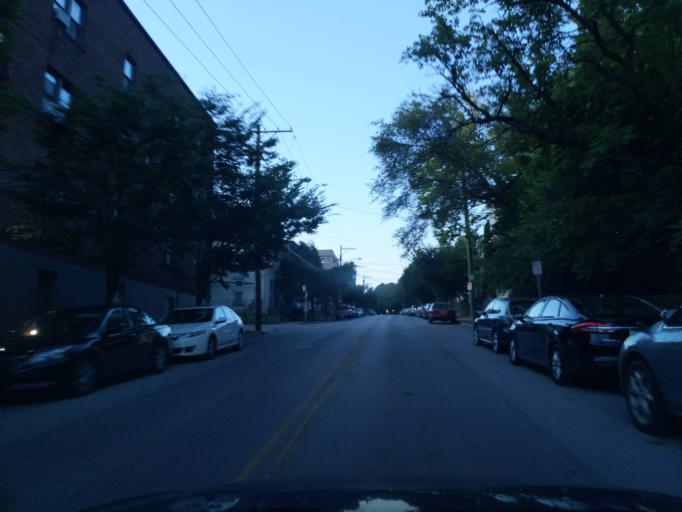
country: US
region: Kentucky
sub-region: Campbell County
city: Newport
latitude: 39.1217
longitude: -84.5206
